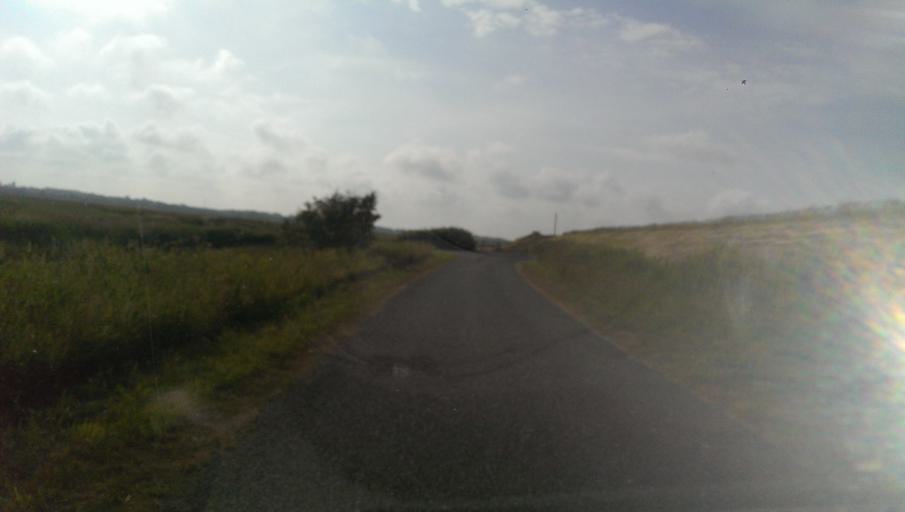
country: DK
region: South Denmark
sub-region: Esbjerg Kommune
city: Tjaereborg
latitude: 55.4327
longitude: 8.6179
